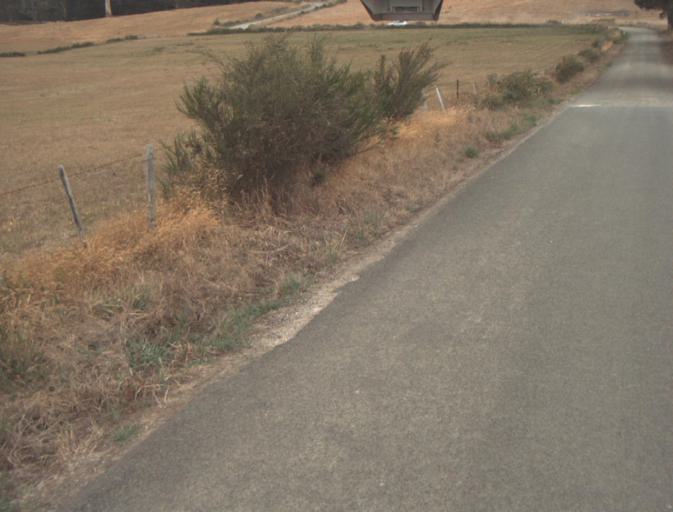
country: AU
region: Tasmania
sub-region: Launceston
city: Mayfield
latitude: -41.1777
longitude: 147.2155
